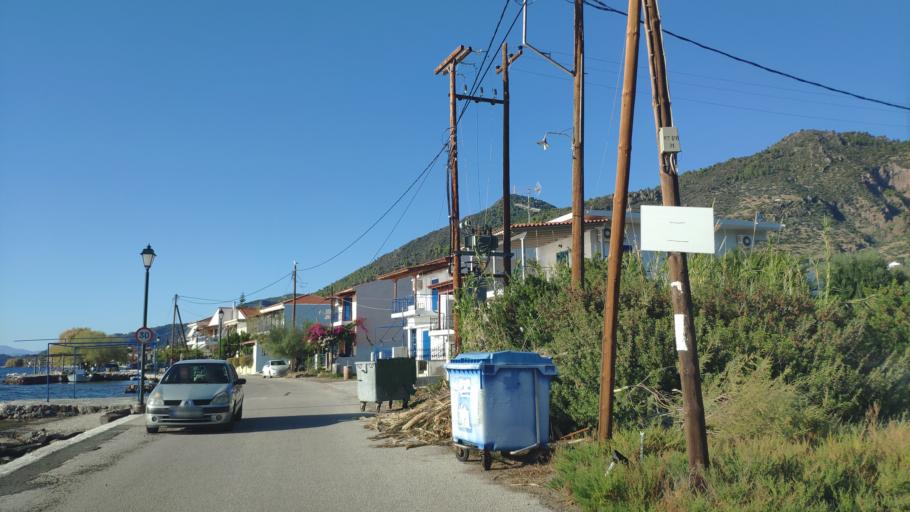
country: GR
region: Attica
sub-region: Nomos Piraios
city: Megalochori
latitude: 37.5864
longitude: 23.3479
